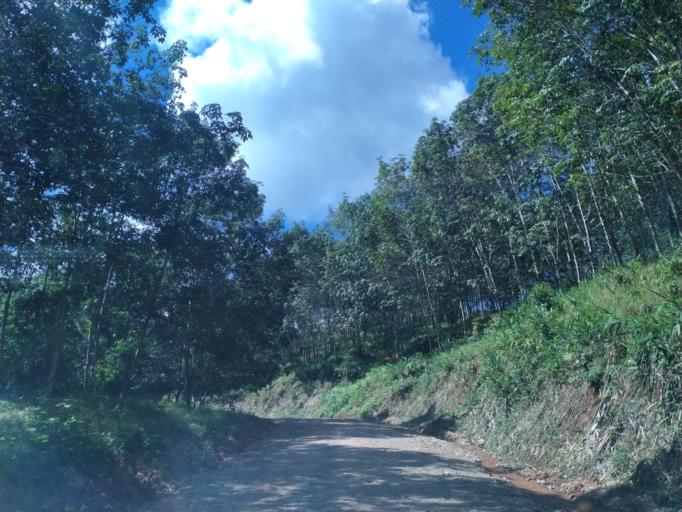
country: TH
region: Nong Khai
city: Rattanawapi
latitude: 18.6378
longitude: 102.9420
